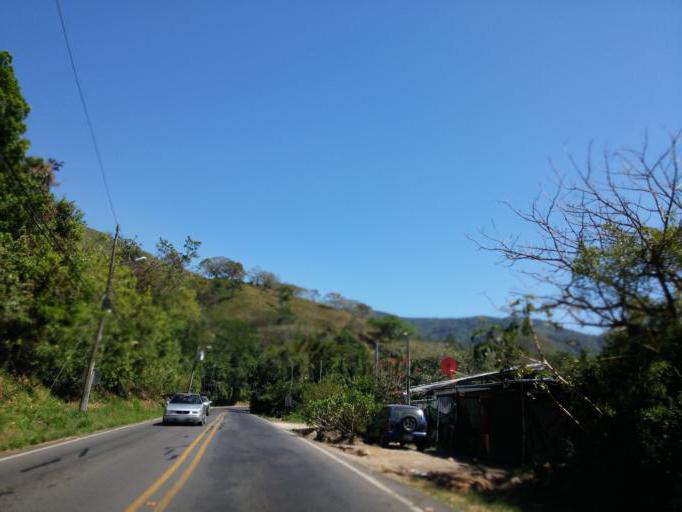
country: CR
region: Heredia
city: Colon
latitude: 9.8939
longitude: -84.2306
